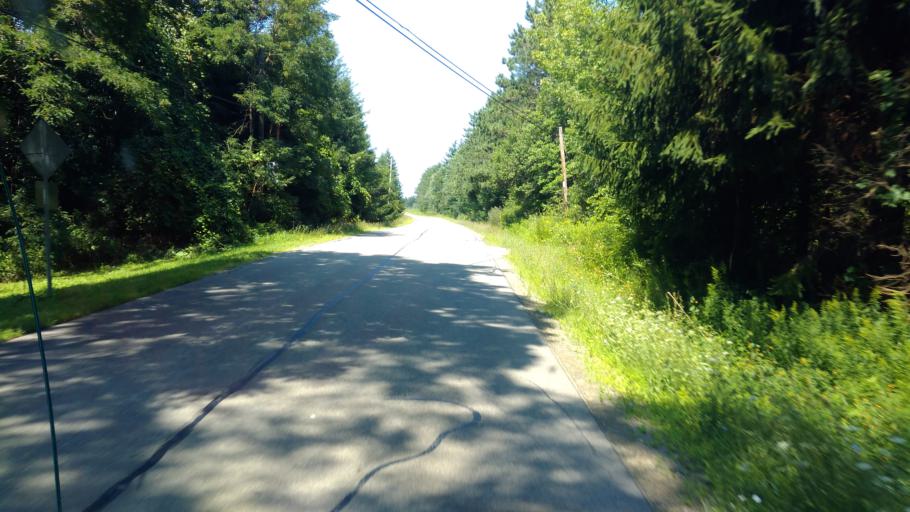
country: US
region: New York
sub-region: Allegany County
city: Belmont
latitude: 42.3086
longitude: -78.0560
